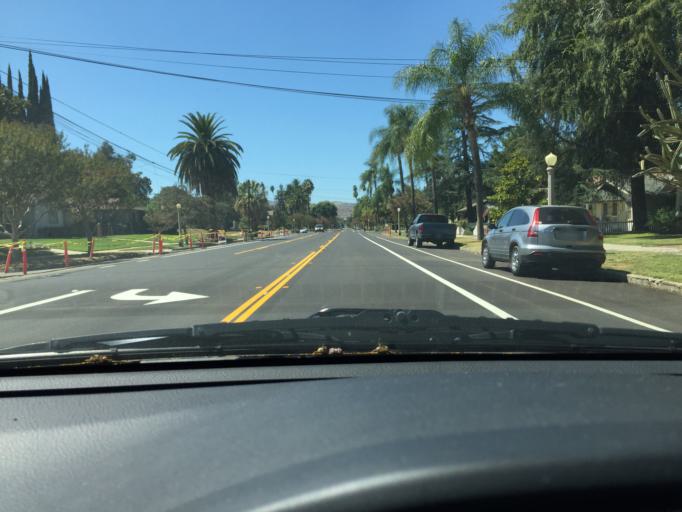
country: US
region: California
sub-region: San Bernardino County
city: Redlands
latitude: 34.0483
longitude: -117.1827
